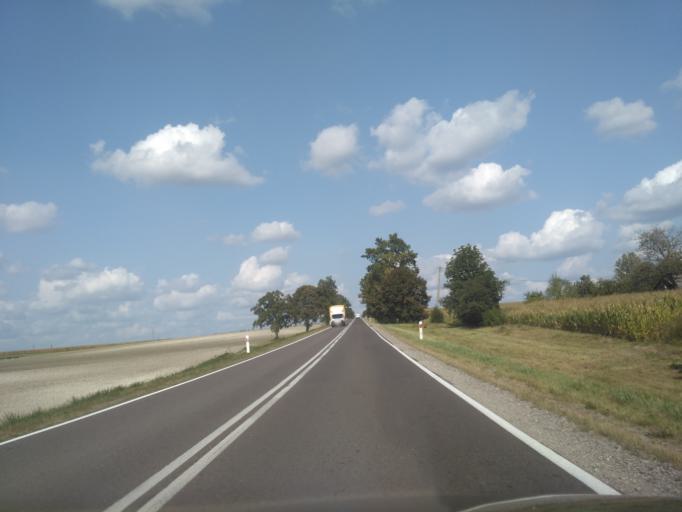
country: PL
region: Lublin Voivodeship
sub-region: Powiat chelmski
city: Rejowiec
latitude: 51.1016
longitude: 23.3040
